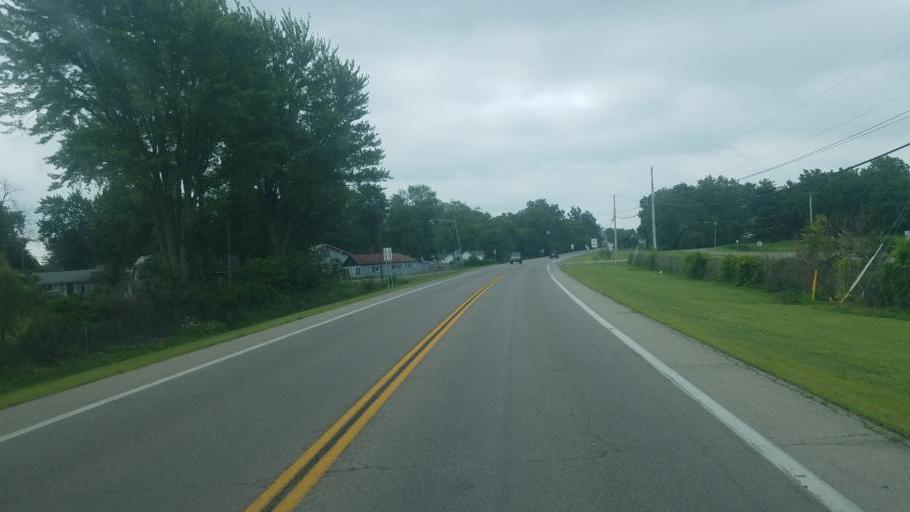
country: US
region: Ohio
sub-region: Logan County
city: Russells Point
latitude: 40.4766
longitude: -83.9004
